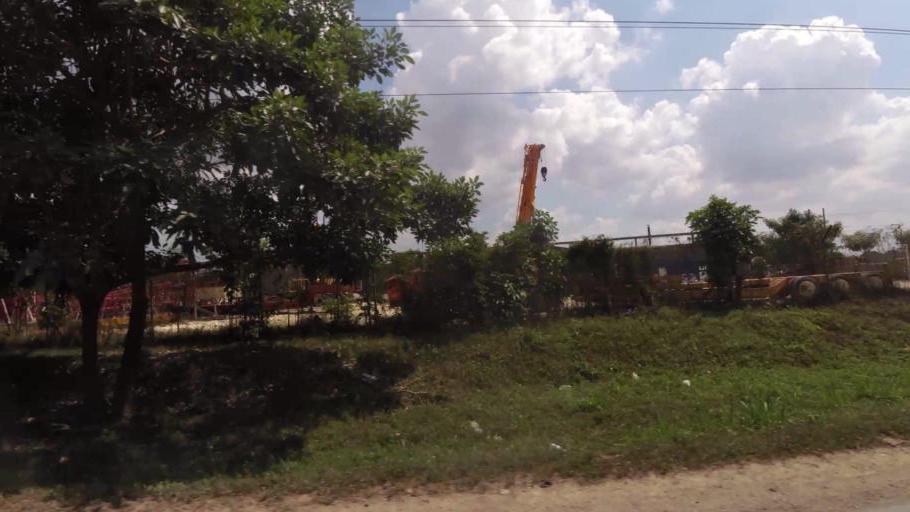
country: CO
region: Bolivar
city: Cartagena
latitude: 10.3501
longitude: -75.4818
